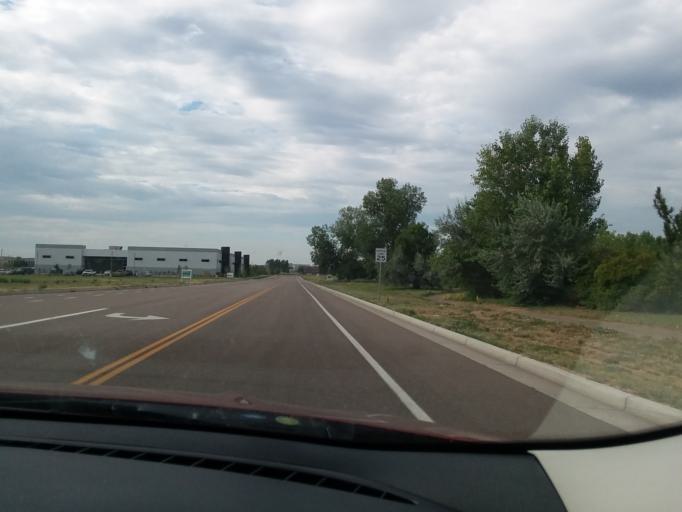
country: US
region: Colorado
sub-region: Larimer County
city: Fort Collins
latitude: 40.5213
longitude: -105.0156
